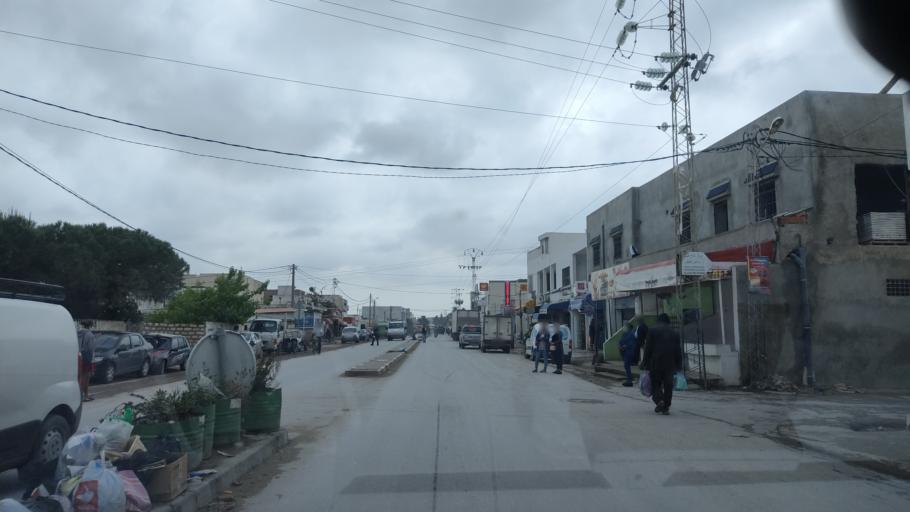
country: TN
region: Ariana
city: Ariana
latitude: 36.8877
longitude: 10.2162
